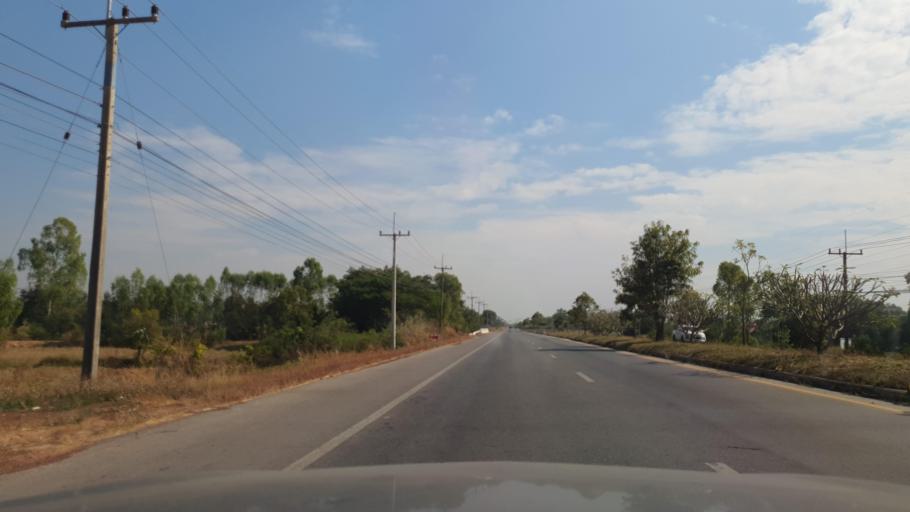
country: TH
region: Maha Sarakham
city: Kantharawichai
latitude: 16.3930
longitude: 103.2903
